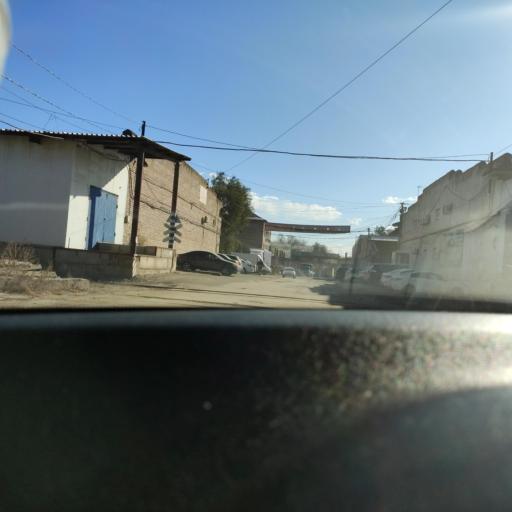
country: RU
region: Samara
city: Petra-Dubrava
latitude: 53.2463
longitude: 50.2996
